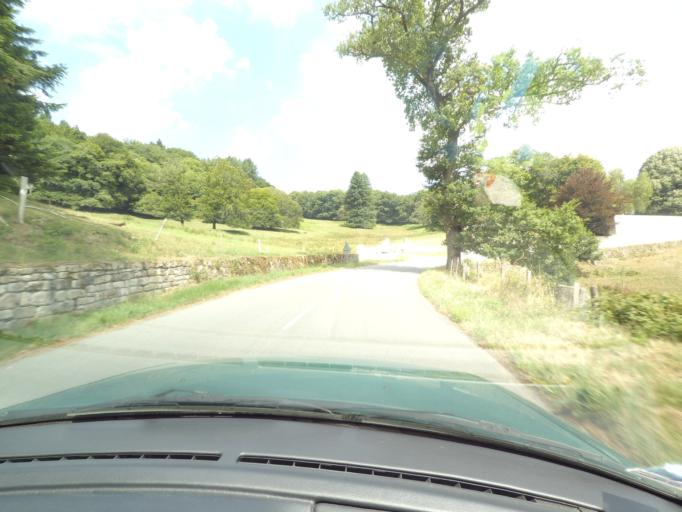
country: FR
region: Limousin
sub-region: Departement de la Haute-Vienne
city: Peyrat-le-Chateau
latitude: 45.7321
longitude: 1.8829
